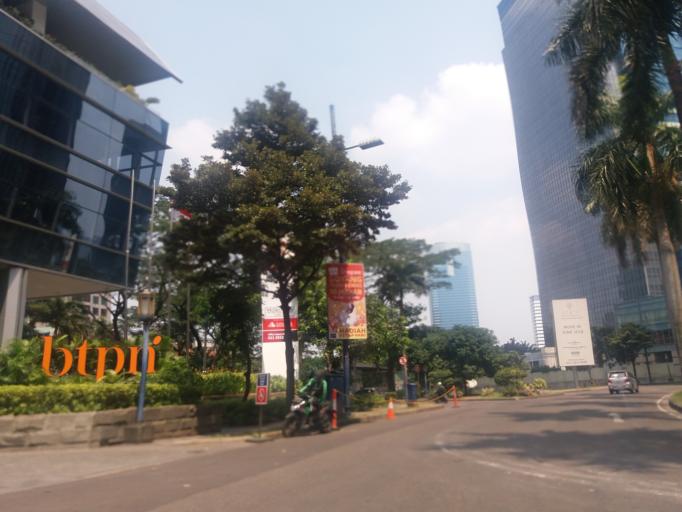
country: ID
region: Jakarta Raya
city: Jakarta
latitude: -6.2295
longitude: 106.8275
